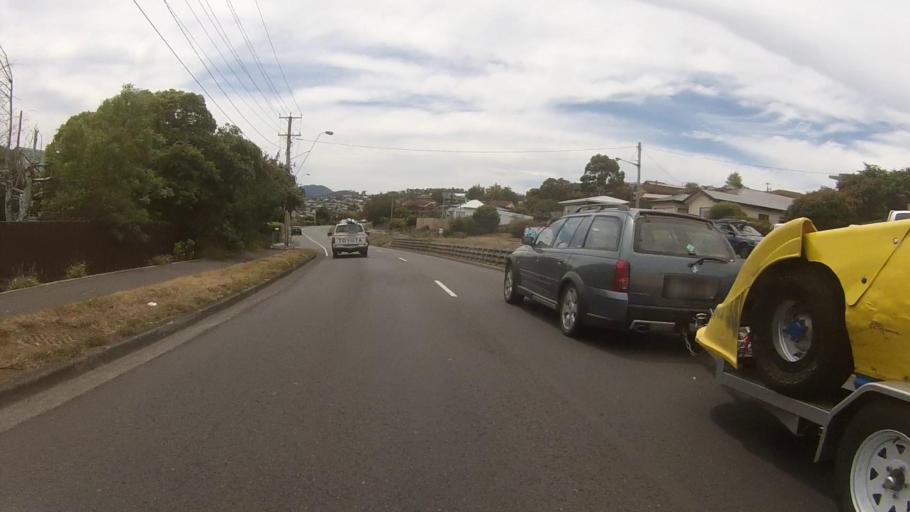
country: AU
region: Tasmania
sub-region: Clarence
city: Lindisfarne
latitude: -42.8566
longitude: 147.3567
